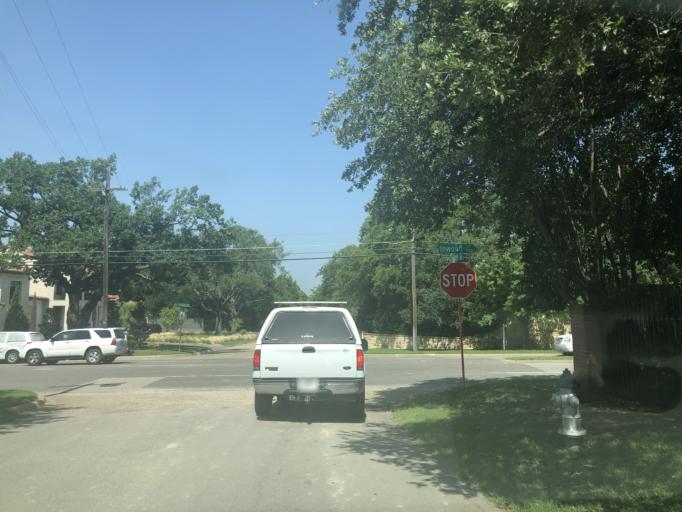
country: US
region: Texas
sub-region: Dallas County
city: University Park
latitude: 32.8710
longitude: -96.8210
